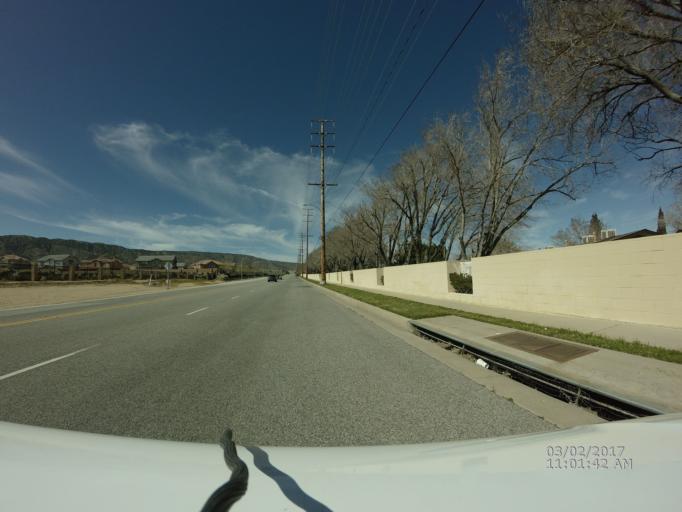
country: US
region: California
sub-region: Los Angeles County
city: Quartz Hill
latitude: 34.6457
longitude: -118.2464
